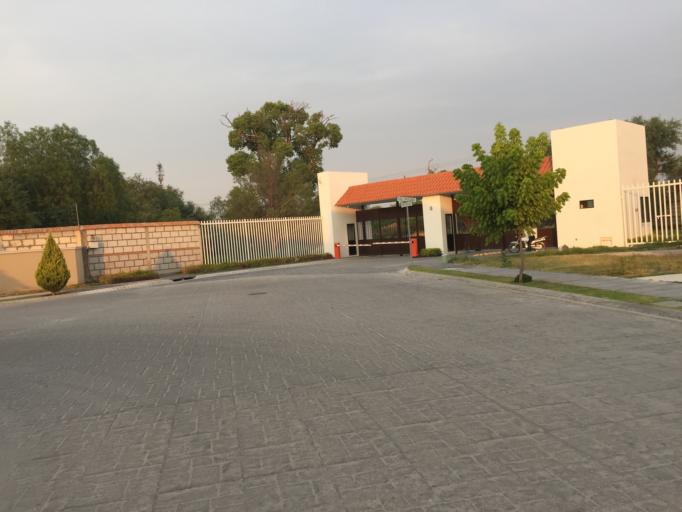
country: MX
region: Aguascalientes
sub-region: Aguascalientes
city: La Loma de los Negritos
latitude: 21.8450
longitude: -102.3550
